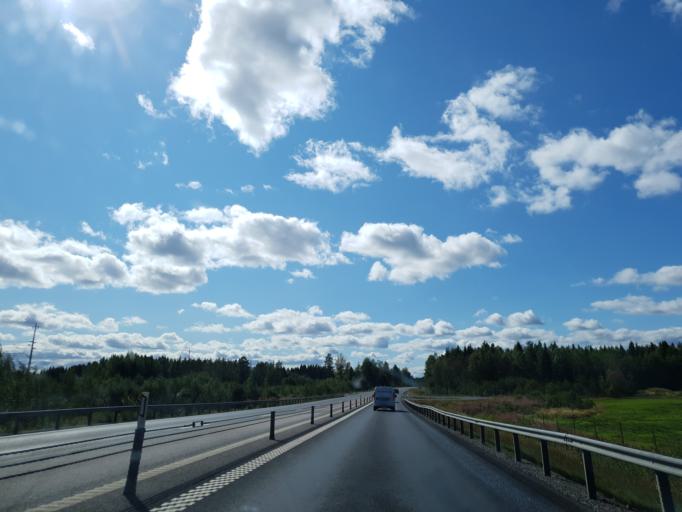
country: SE
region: Vaesterbotten
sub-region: Nordmalings Kommun
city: Nordmaling
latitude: 63.5058
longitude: 19.3473
